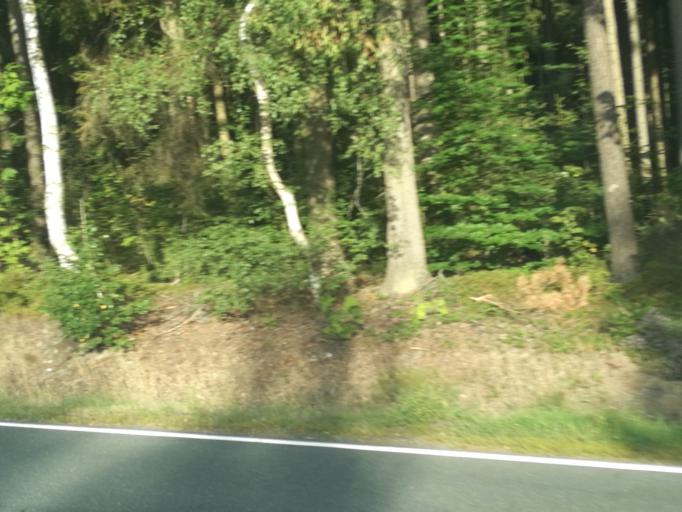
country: DE
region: Saxony
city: Eichigt
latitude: 50.3354
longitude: 12.1631
